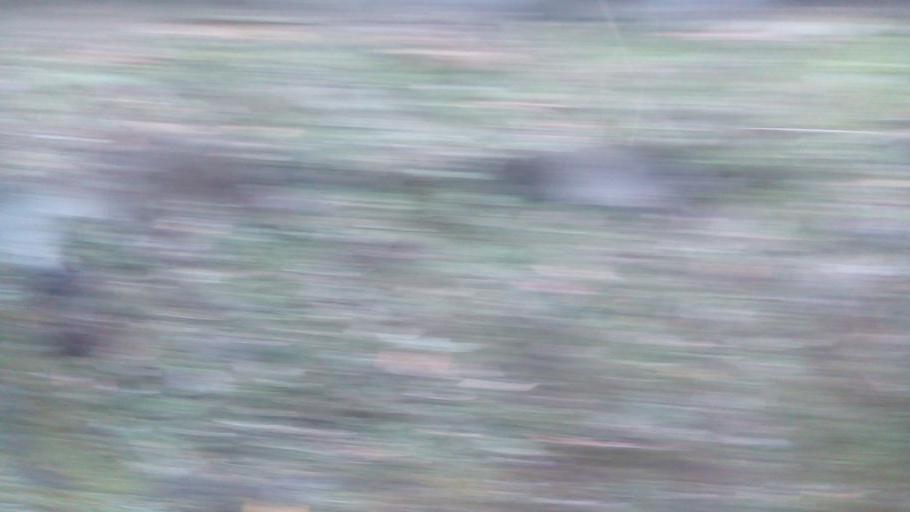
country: TW
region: Taiwan
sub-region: Yilan
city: Yilan
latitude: 24.5666
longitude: 121.4726
